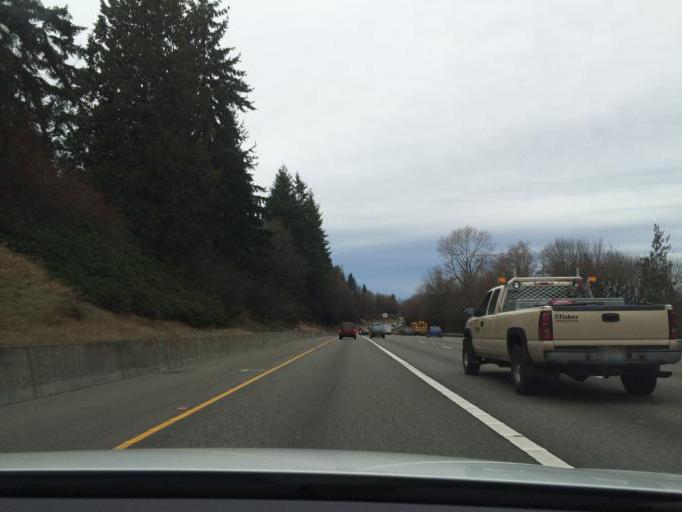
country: US
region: Washington
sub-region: Snohomish County
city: Everett
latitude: 47.9356
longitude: -122.1962
